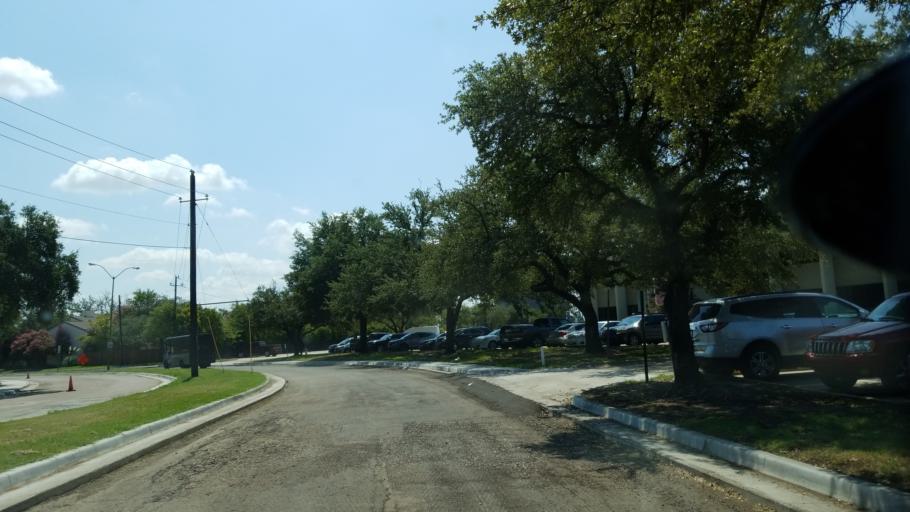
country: US
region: Texas
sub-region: Dallas County
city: Richardson
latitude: 32.9182
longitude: -96.7399
